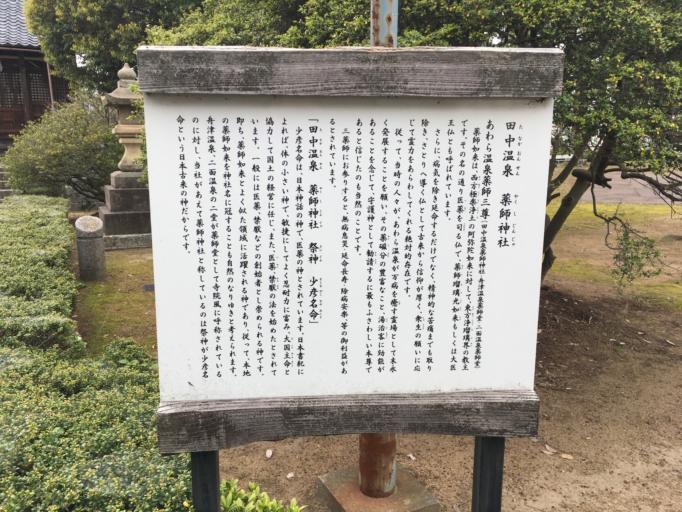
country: JP
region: Fukui
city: Mikuni
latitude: 36.2244
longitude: 136.1899
